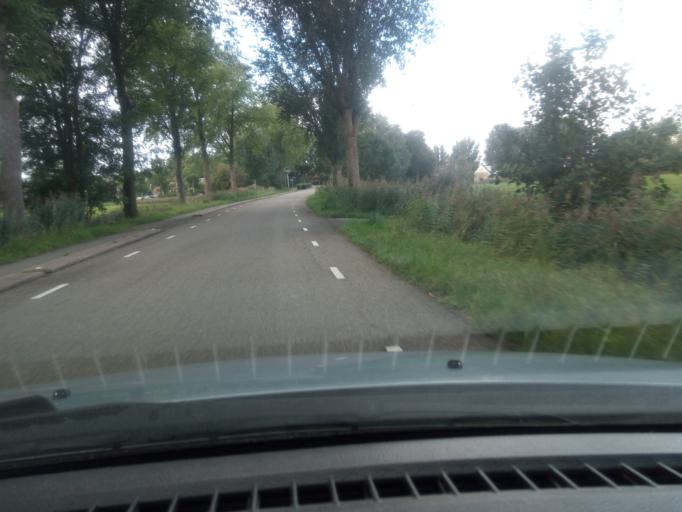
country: NL
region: Groningen
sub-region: Gemeente Zuidhorn
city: Grijpskerk
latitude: 53.2667
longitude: 6.2542
